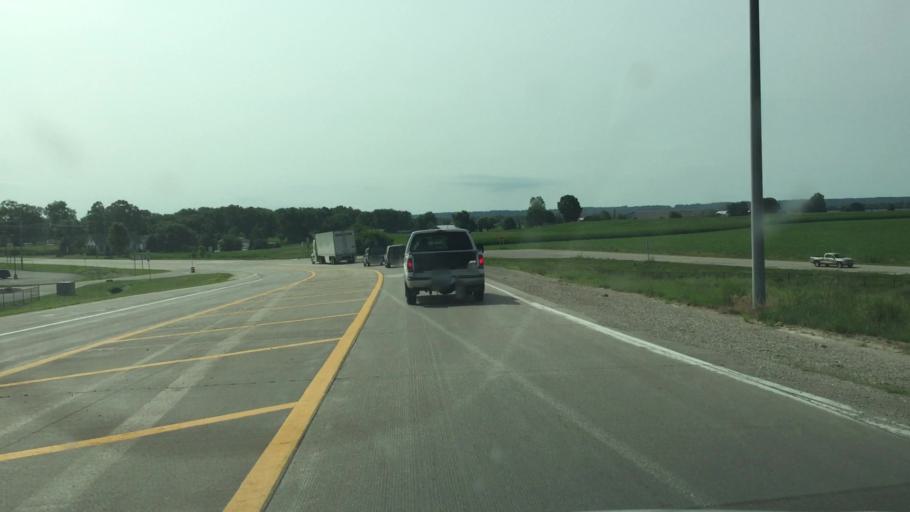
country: US
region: Illinois
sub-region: Hancock County
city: Nauvoo
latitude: 40.6252
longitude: -91.3971
